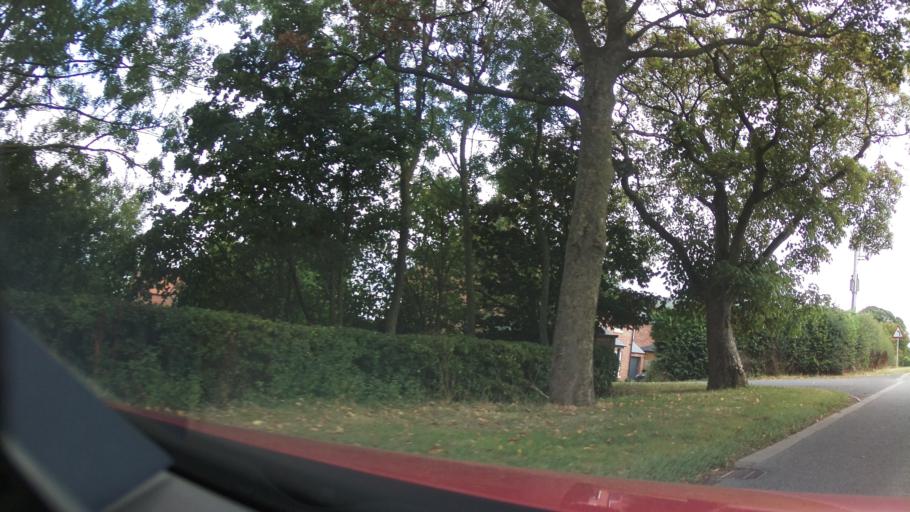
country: GB
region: England
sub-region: North Yorkshire
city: Ripon
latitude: 54.1505
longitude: -1.5315
